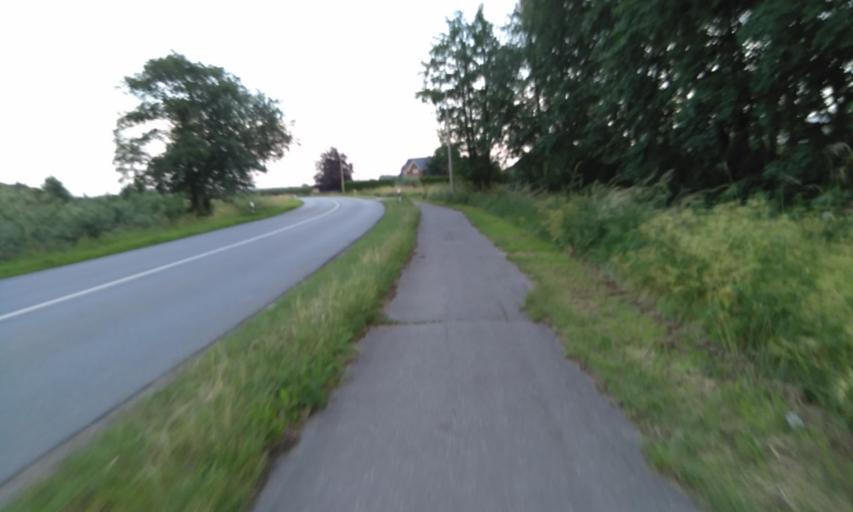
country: DE
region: Lower Saxony
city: Jork
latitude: 53.5126
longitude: 9.7196
